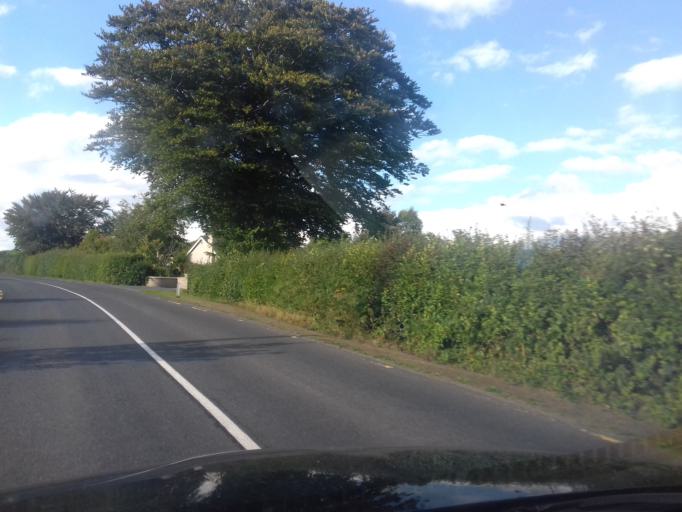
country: IE
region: Leinster
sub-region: Loch Garman
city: New Ross
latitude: 52.4471
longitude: -6.9625
